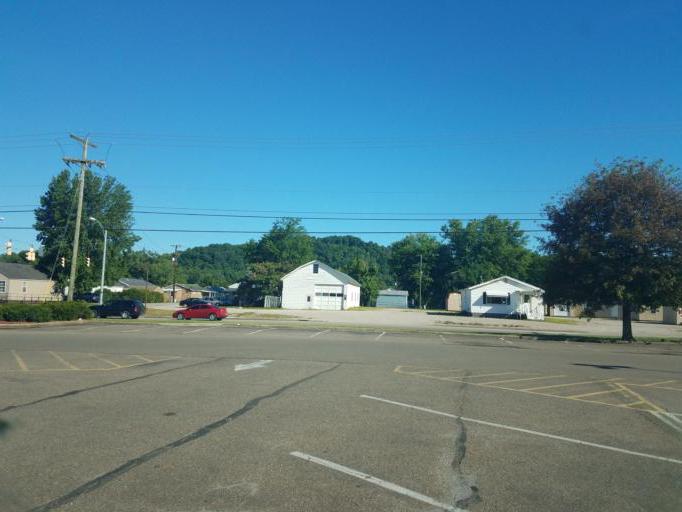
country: US
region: Ohio
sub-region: Gallia County
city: Gallipolis
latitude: 38.8228
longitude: -82.1733
